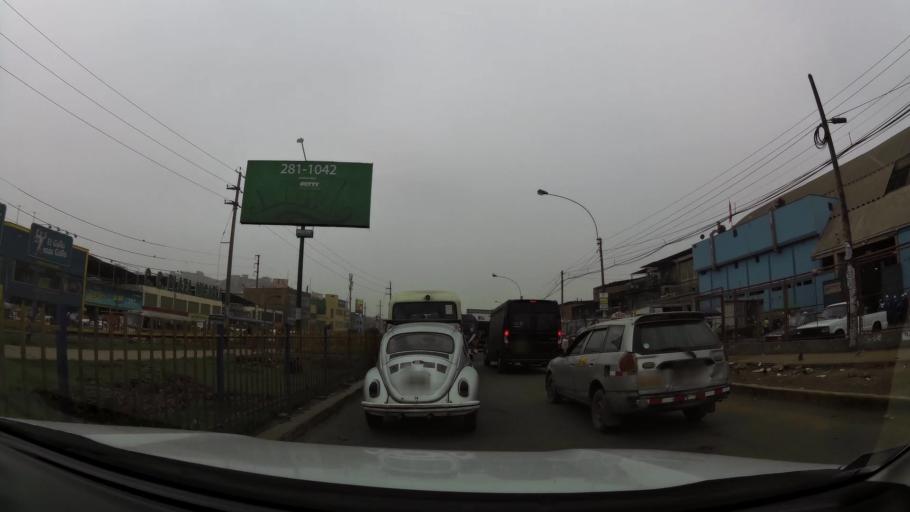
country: PE
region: Lima
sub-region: Lima
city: Surco
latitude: -12.1735
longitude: -76.9477
